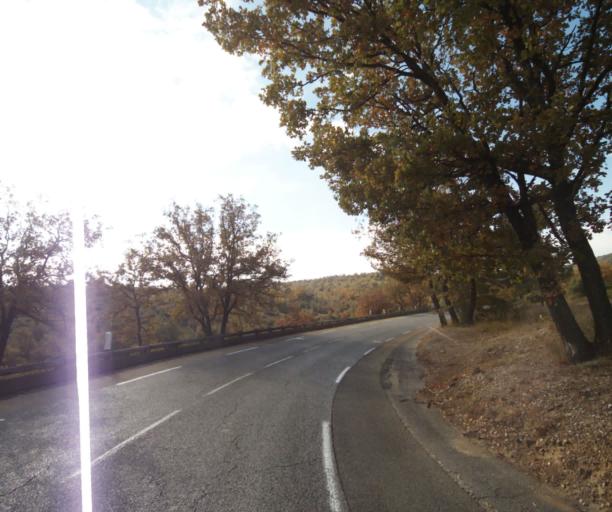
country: FR
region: Provence-Alpes-Cote d'Azur
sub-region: Departement des Bouches-du-Rhone
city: Cadolive
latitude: 43.3832
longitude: 5.5481
